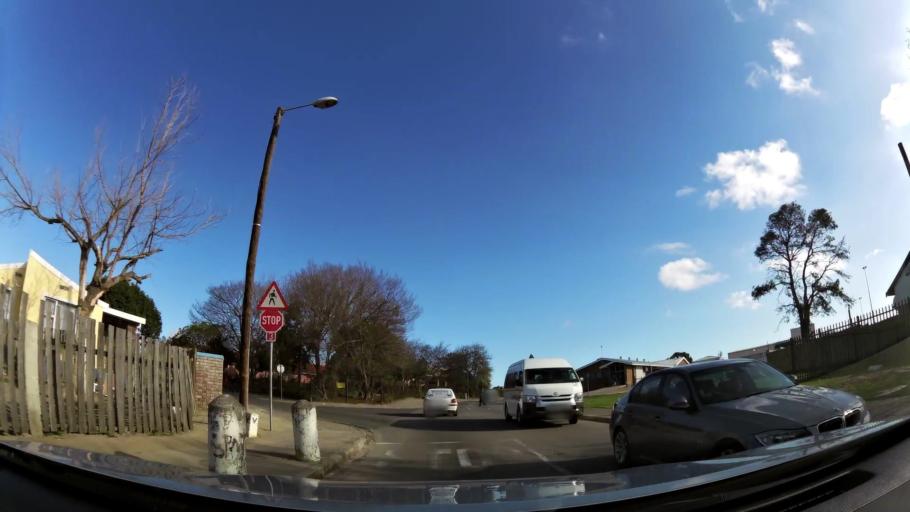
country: ZA
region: Western Cape
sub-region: Eden District Municipality
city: George
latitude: -33.9816
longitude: 22.4750
